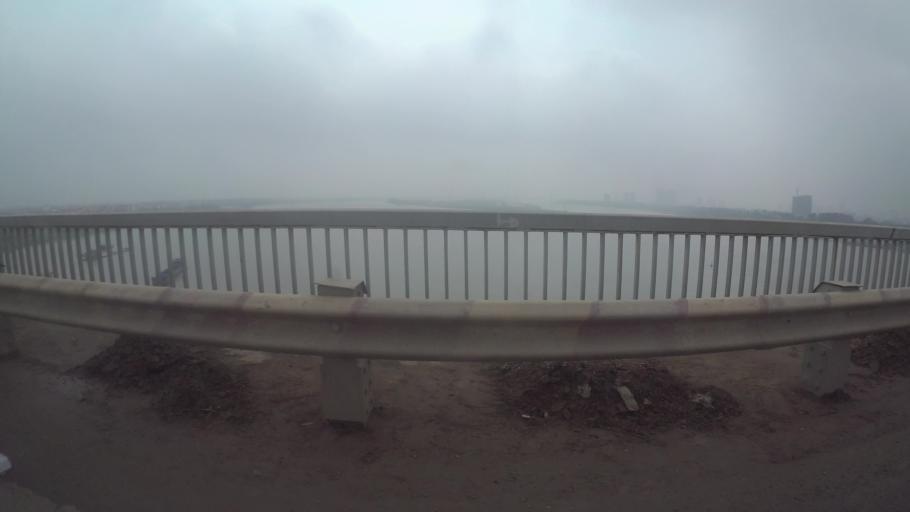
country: VN
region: Ha Noi
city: Tay Ho
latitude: 21.0985
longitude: 105.7866
